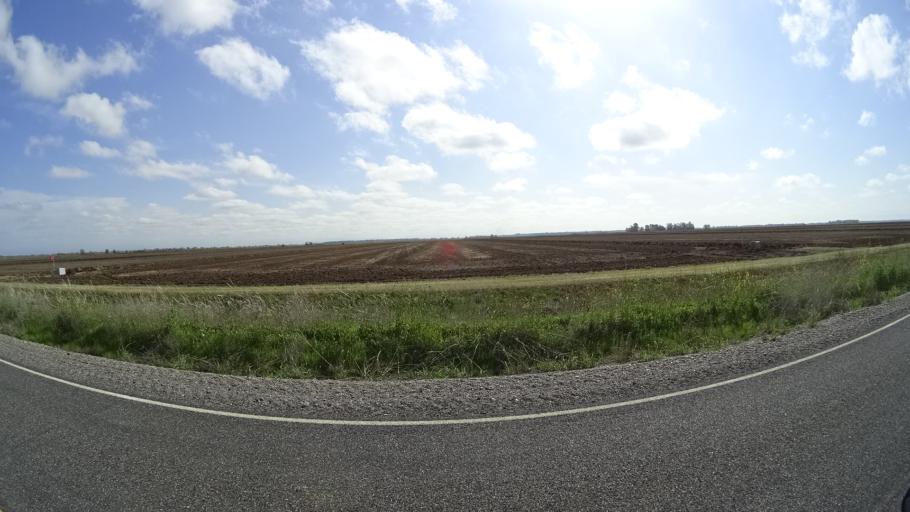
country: US
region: California
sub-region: Butte County
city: Durham
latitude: 39.5110
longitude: -121.9299
